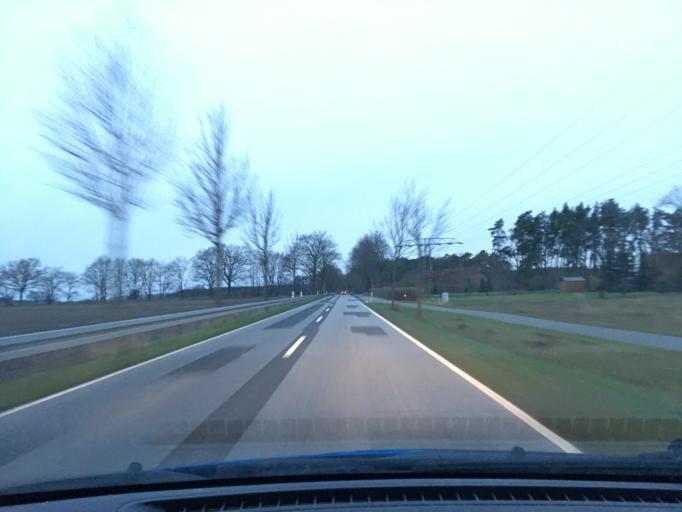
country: DE
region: Mecklenburg-Vorpommern
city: Boizenburg
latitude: 53.3599
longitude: 10.7849
